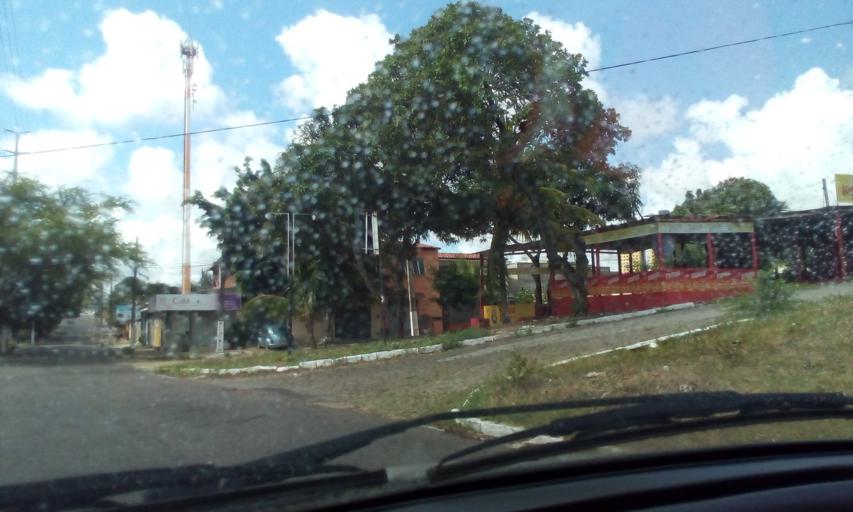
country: BR
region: Rio Grande do Norte
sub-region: Natal
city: Natal
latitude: -5.8677
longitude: -35.2076
